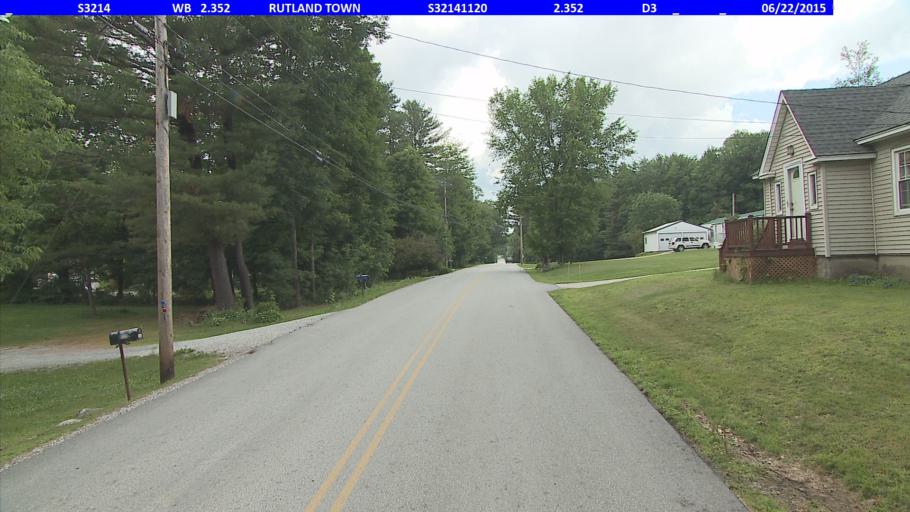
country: US
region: Vermont
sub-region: Rutland County
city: Rutland
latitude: 43.6314
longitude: -72.9435
